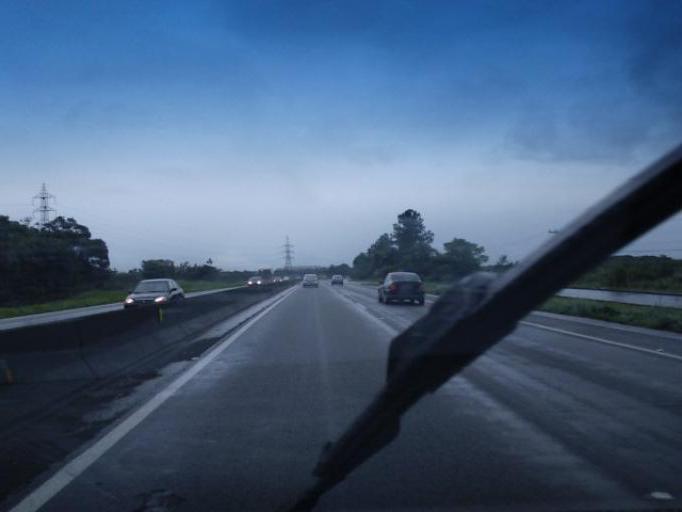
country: BR
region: Santa Catarina
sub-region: Barra Velha
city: Barra Velha
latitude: -26.4967
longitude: -48.7318
